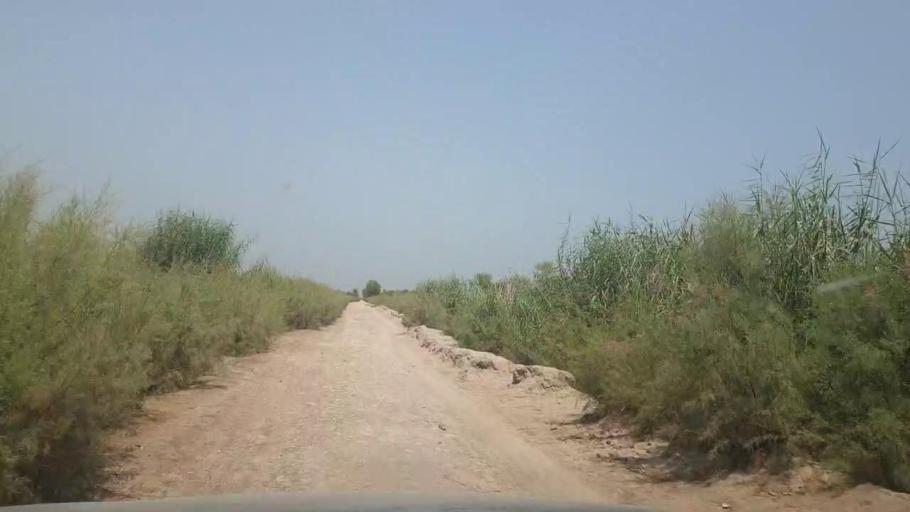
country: PK
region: Sindh
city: Lakhi
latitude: 27.8332
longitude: 68.6238
